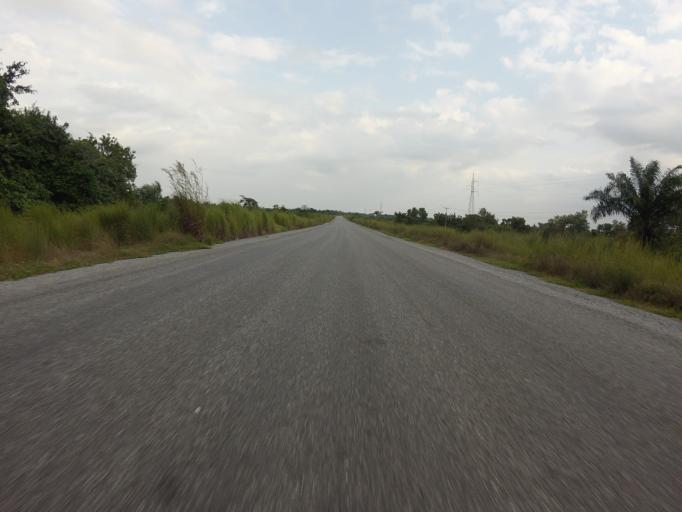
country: GH
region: Volta
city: Ho
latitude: 6.4095
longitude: 0.5224
